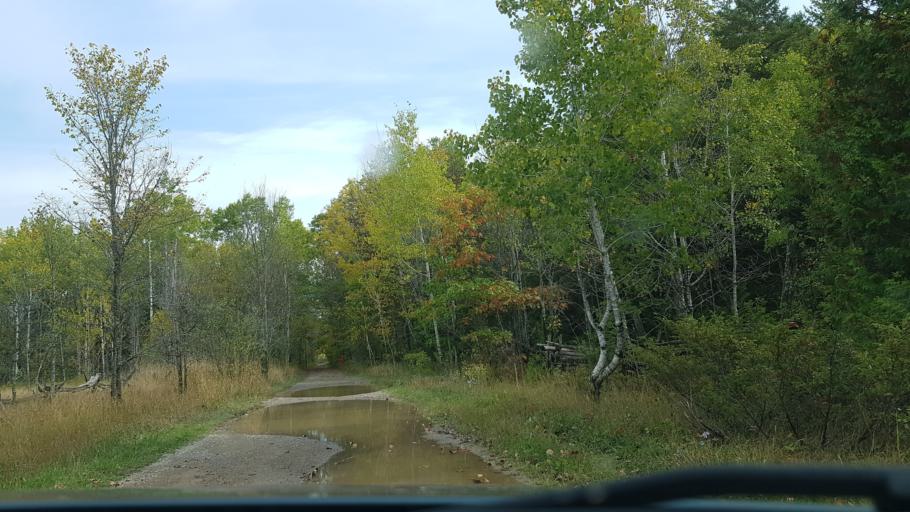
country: CA
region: Ontario
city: Orillia
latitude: 44.6921
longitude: -79.0226
